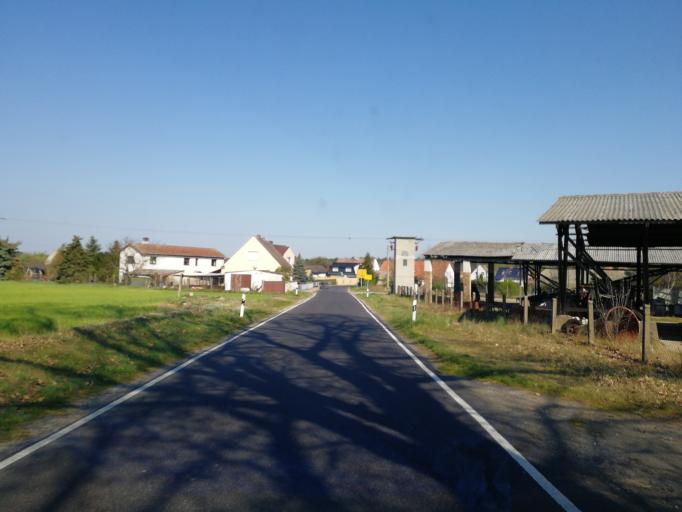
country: DE
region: Brandenburg
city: Bronkow
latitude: 51.7204
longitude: 13.8591
